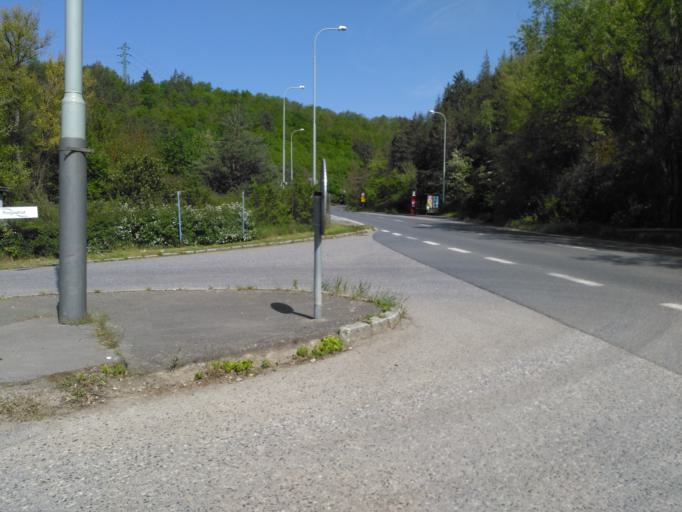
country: CZ
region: Central Bohemia
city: Cernosice
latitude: 49.9973
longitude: 14.3421
